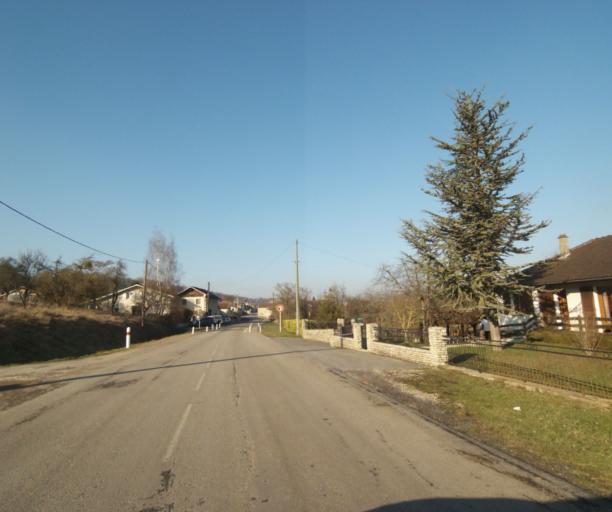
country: FR
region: Champagne-Ardenne
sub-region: Departement de la Haute-Marne
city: Chevillon
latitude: 48.5038
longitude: 5.1157
